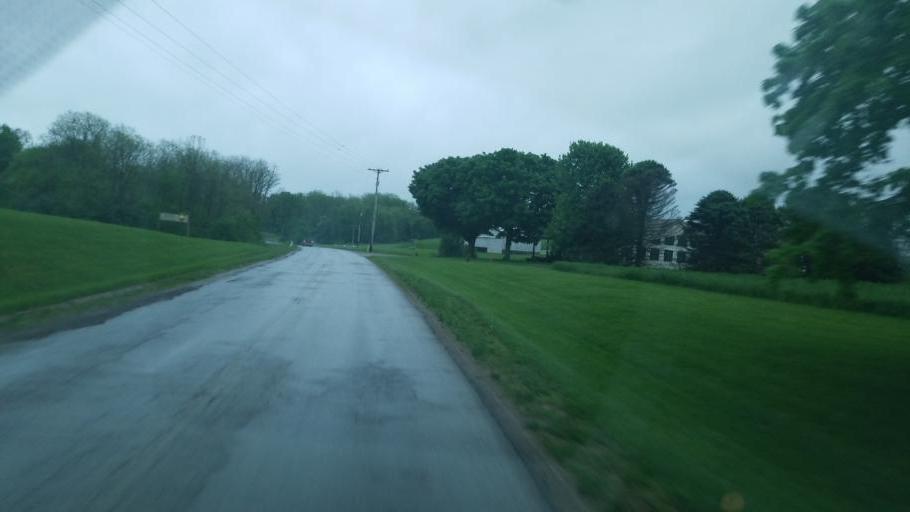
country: US
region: Ohio
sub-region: Highland County
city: Greenfield
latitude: 39.2967
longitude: -83.4633
